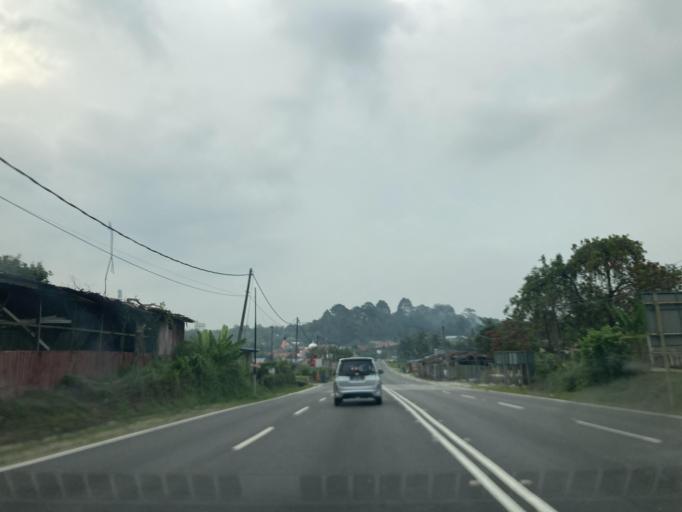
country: MY
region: Selangor
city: Kuang
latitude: 3.2093
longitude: 101.5374
